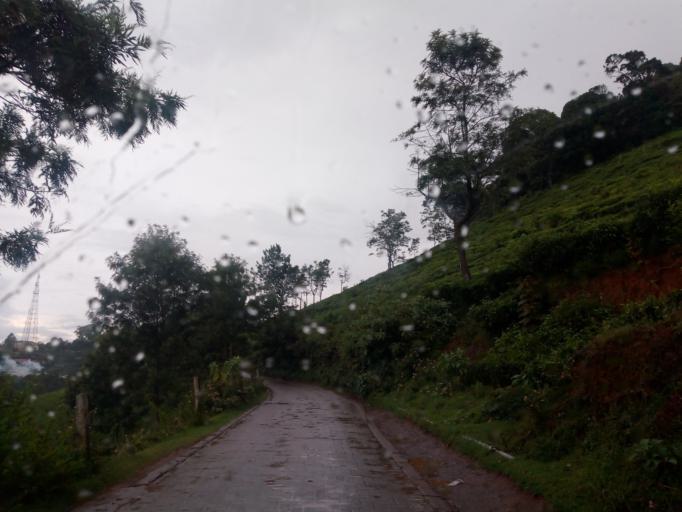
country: IN
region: Tamil Nadu
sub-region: Nilgiri
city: Wellington
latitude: 11.3488
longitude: 76.8154
